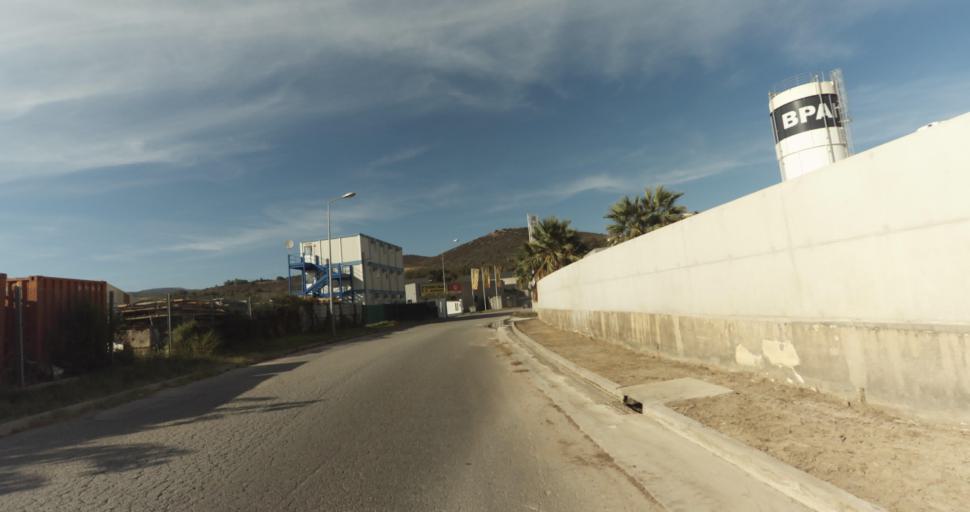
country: FR
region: Corsica
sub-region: Departement de la Corse-du-Sud
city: Ajaccio
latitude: 41.9314
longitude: 8.7871
